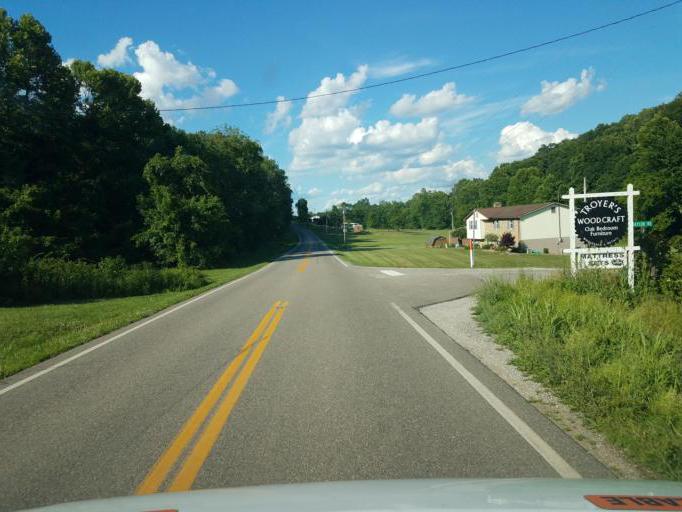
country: US
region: Ohio
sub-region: Gallia County
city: Gallipolis
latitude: 38.7813
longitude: -82.3475
